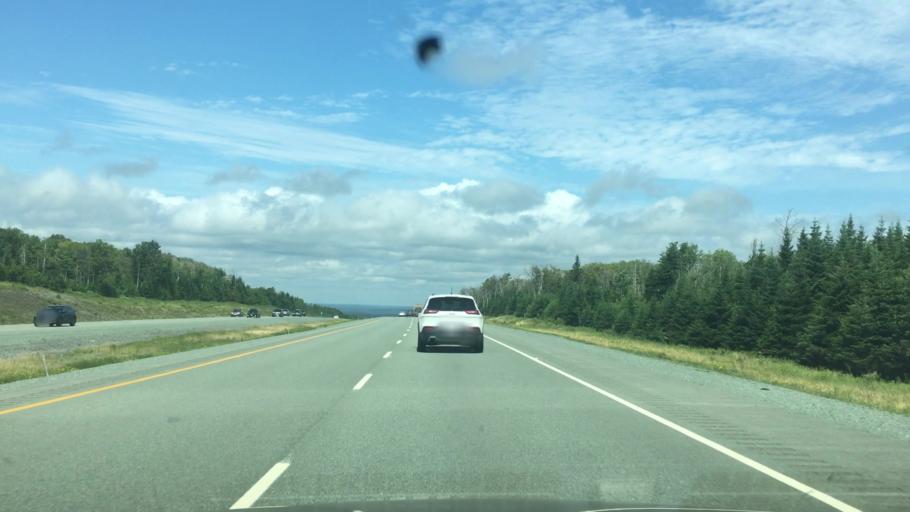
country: CA
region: Nova Scotia
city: Oxford
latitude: 45.5823
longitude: -63.7168
